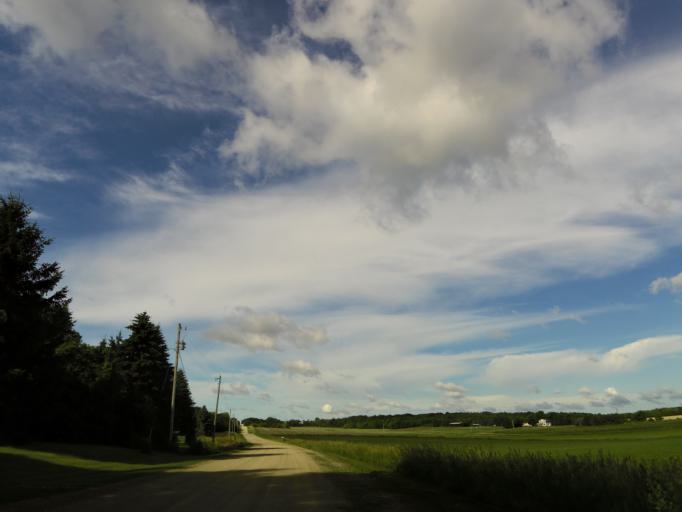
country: US
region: Minnesota
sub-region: Goodhue County
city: Cannon Falls
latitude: 44.6181
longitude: -92.9718
